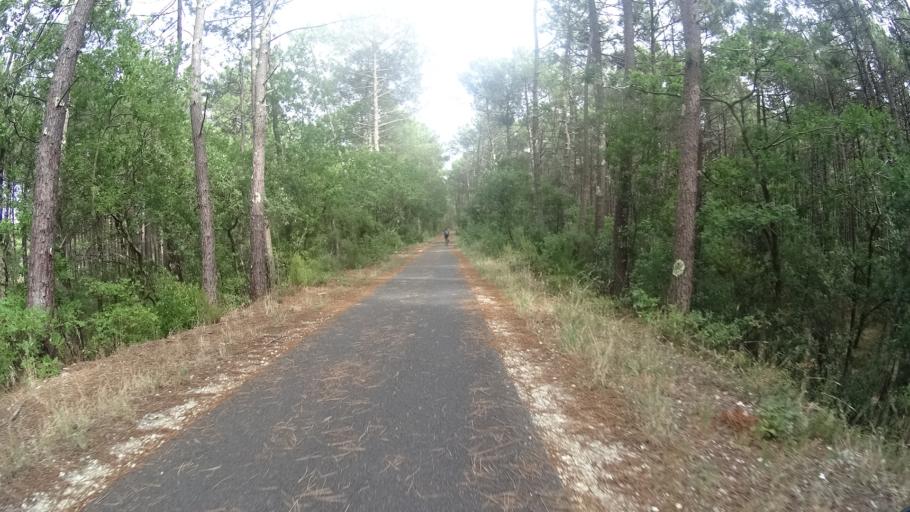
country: FR
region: Aquitaine
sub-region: Departement de la Gironde
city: Lacanau
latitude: 45.0067
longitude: -1.1424
